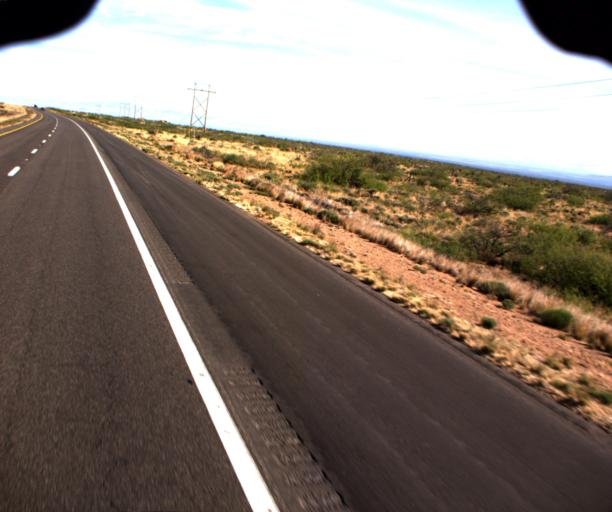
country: US
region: Arizona
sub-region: Graham County
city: Swift Trail Junction
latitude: 32.5240
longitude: -109.6734
